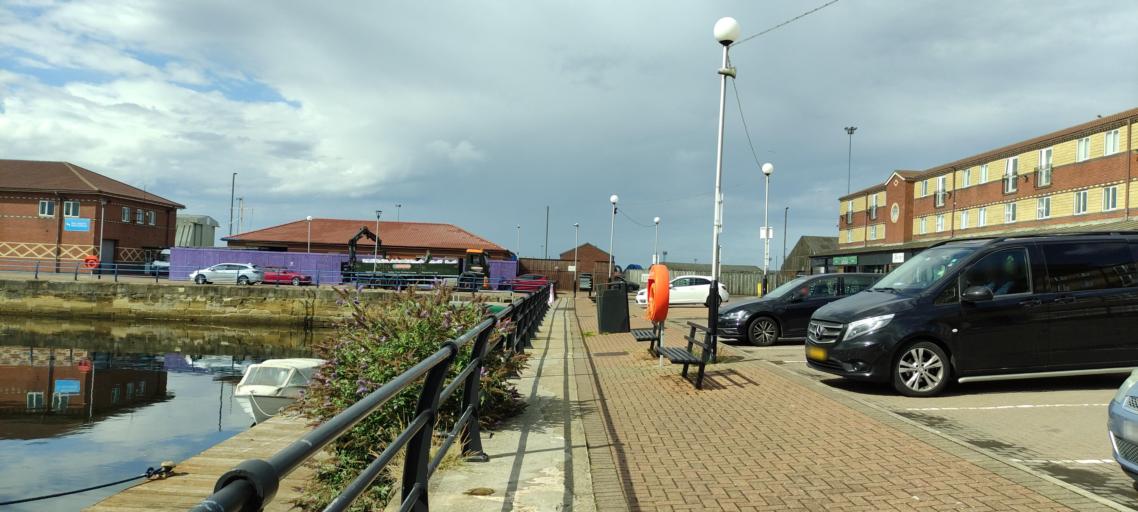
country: GB
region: England
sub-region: Hartlepool
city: Hartlepool
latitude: 54.6927
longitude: -1.1988
